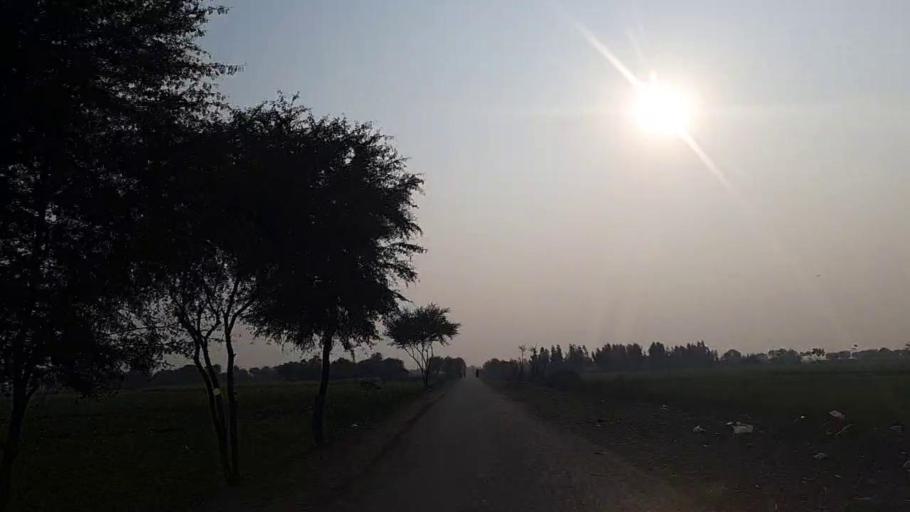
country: PK
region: Sindh
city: Nawabshah
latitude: 26.2243
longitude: 68.4789
